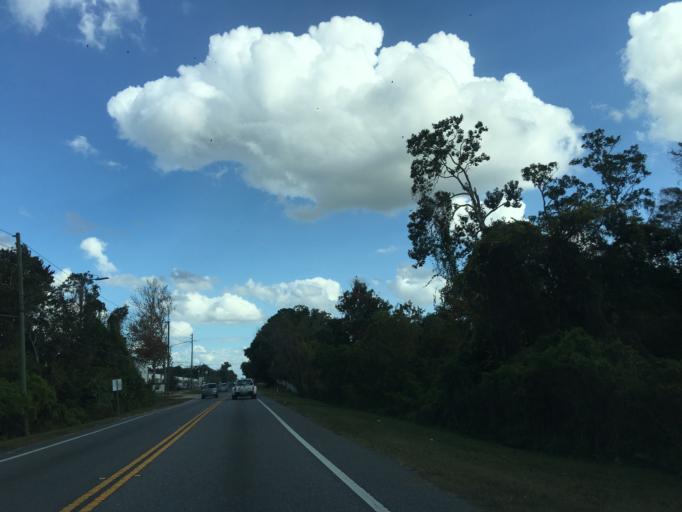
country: US
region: Florida
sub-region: Orange County
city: Eatonville
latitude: 28.6184
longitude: -81.4080
